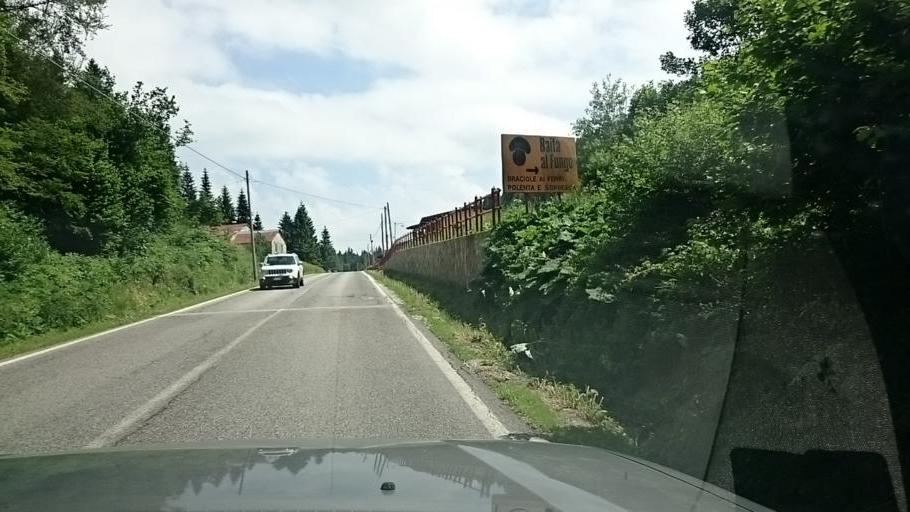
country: IT
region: Veneto
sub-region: Provincia di Vicenza
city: Conco
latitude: 45.8350
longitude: 11.5924
